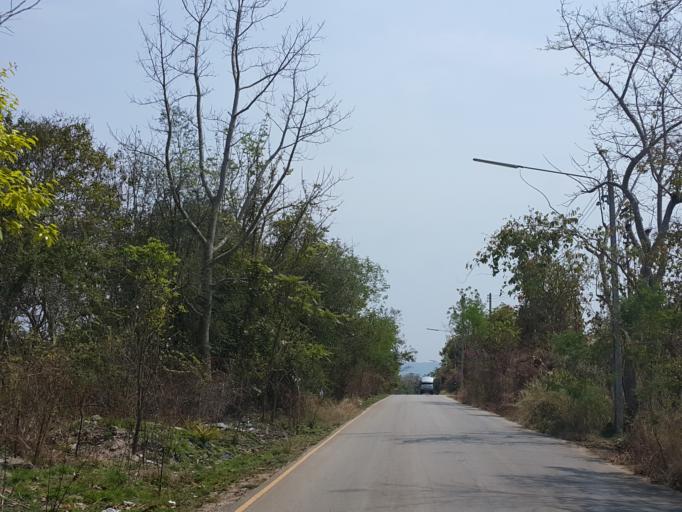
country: TH
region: Lampang
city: Lampang
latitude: 18.3062
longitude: 99.4234
